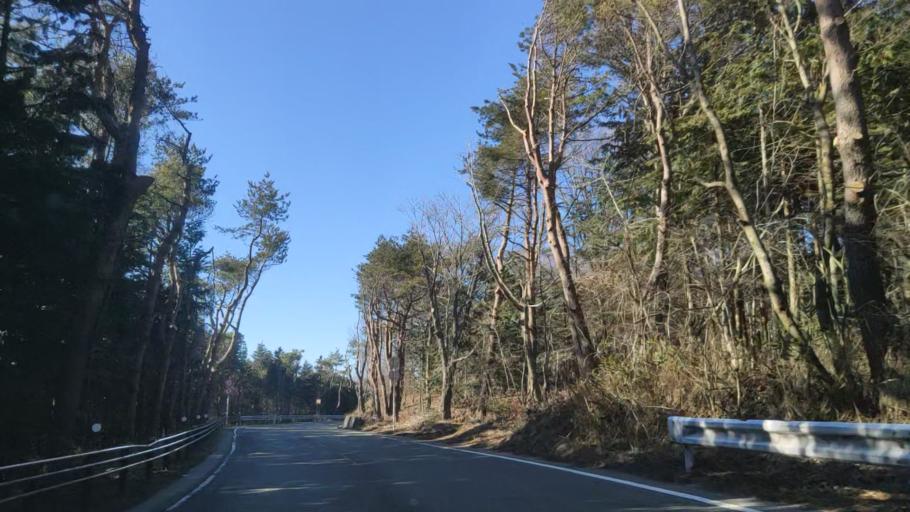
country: JP
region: Yamanashi
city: Fujikawaguchiko
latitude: 35.4391
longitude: 138.6365
